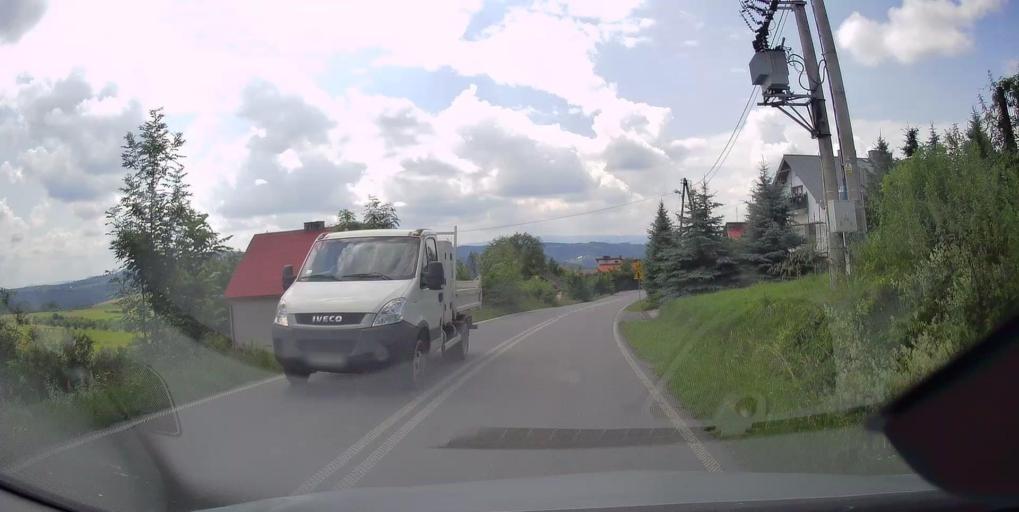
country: PL
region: Lesser Poland Voivodeship
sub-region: Powiat nowosadecki
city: Korzenna
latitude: 49.6890
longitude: 20.7762
